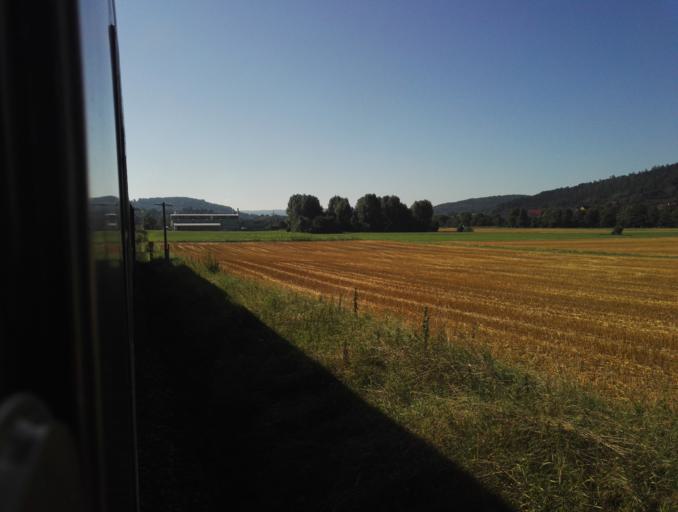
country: DE
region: Baden-Wuerttemberg
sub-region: Regierungsbezirk Stuttgart
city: Rudersberg
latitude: 48.8659
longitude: 9.5314
